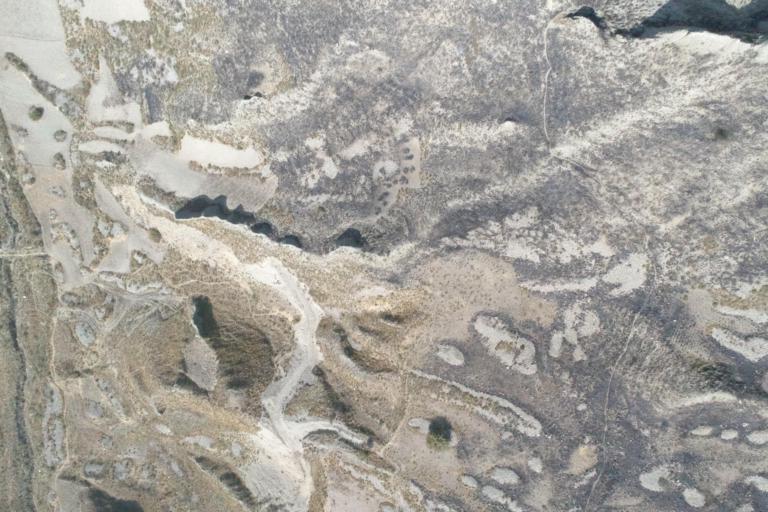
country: BO
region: La Paz
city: La Paz
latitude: -16.4718
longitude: -68.0950
